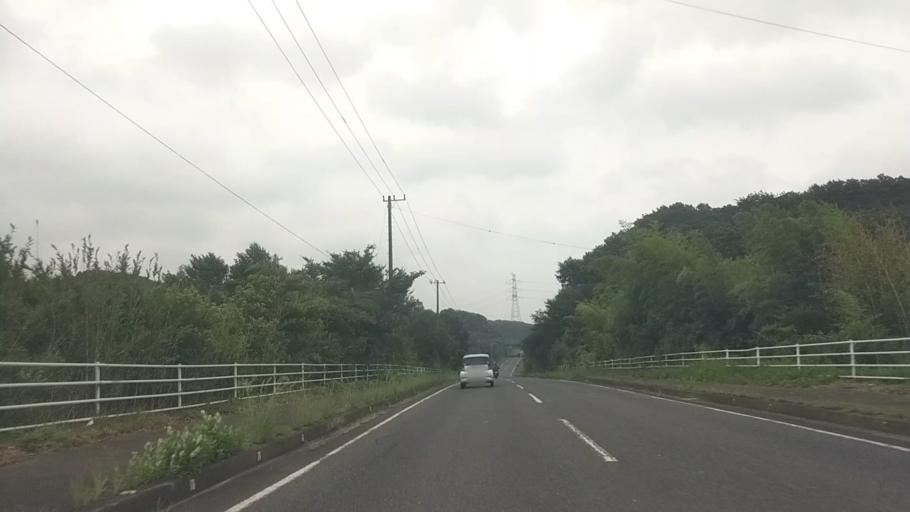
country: JP
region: Chiba
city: Kisarazu
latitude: 35.3878
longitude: 139.9932
